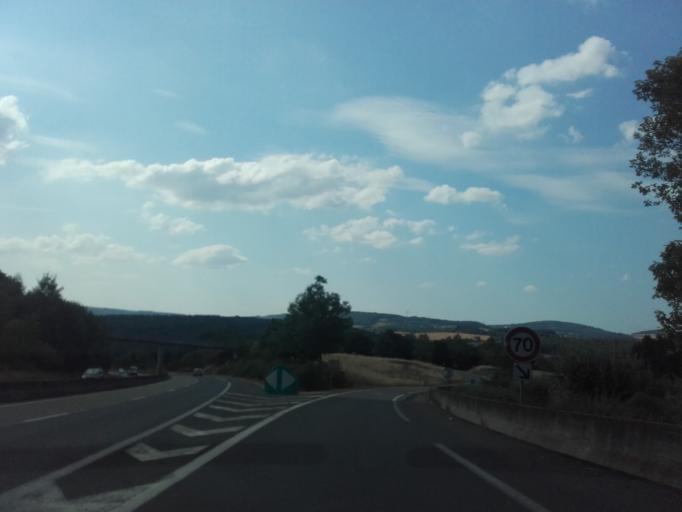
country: FR
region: Bourgogne
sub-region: Departement de Saone-et-Loire
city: Cluny
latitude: 46.3956
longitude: 4.6529
